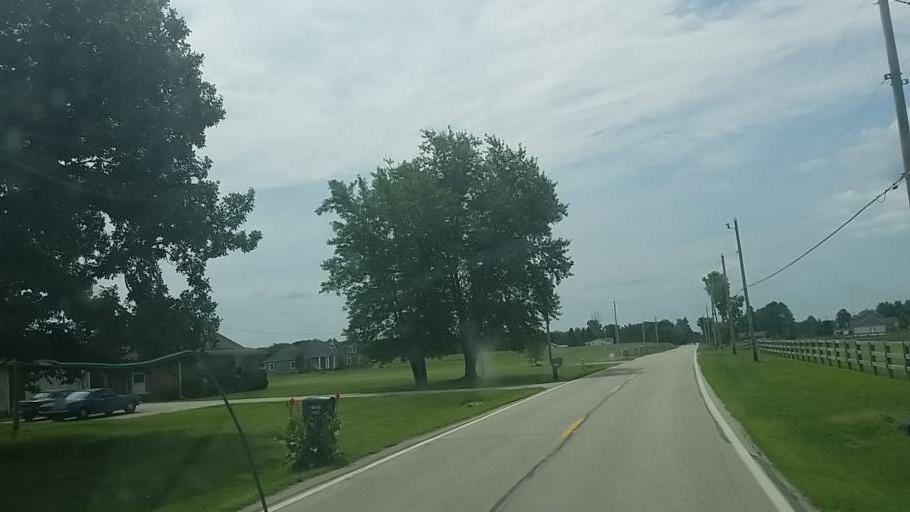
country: US
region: Ohio
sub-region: Delaware County
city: Sunbury
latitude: 40.1950
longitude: -82.8258
